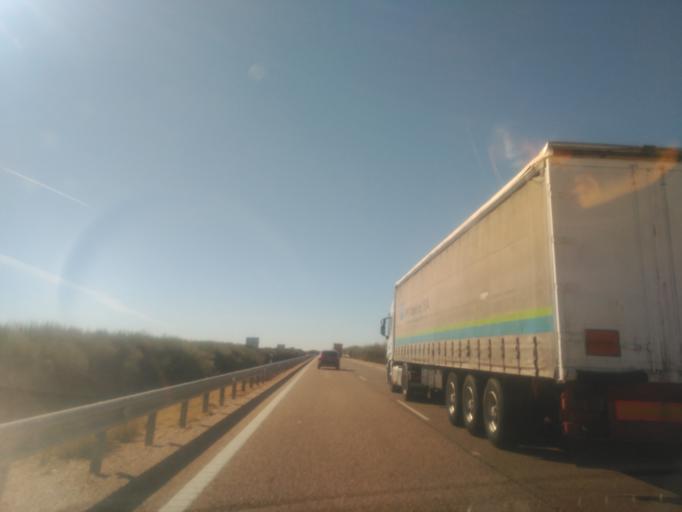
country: ES
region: Castille and Leon
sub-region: Provincia de Valladolid
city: Alaejos
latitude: 41.2936
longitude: -5.2356
